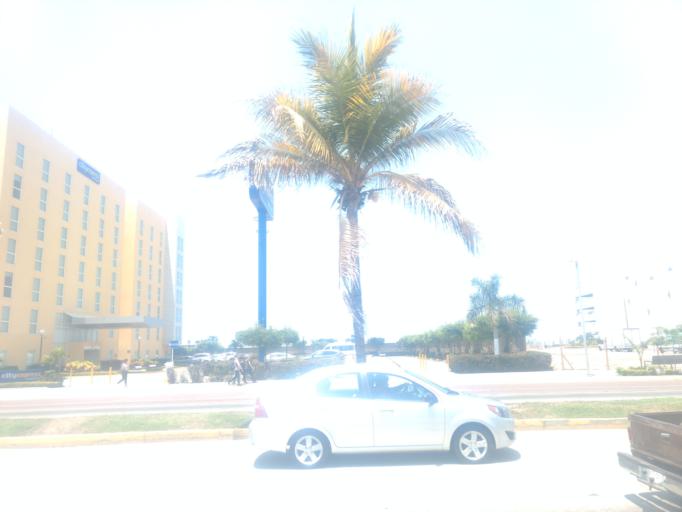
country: MX
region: Colima
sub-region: Manzanillo
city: Manzanillo
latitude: 19.0998
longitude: -104.3243
